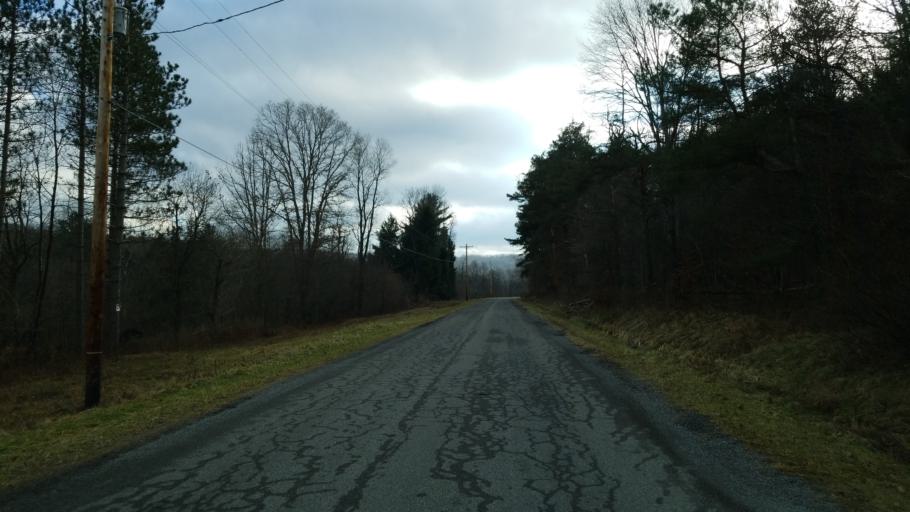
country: US
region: Pennsylvania
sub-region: Clearfield County
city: Treasure Lake
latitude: 41.1347
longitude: -78.6031
